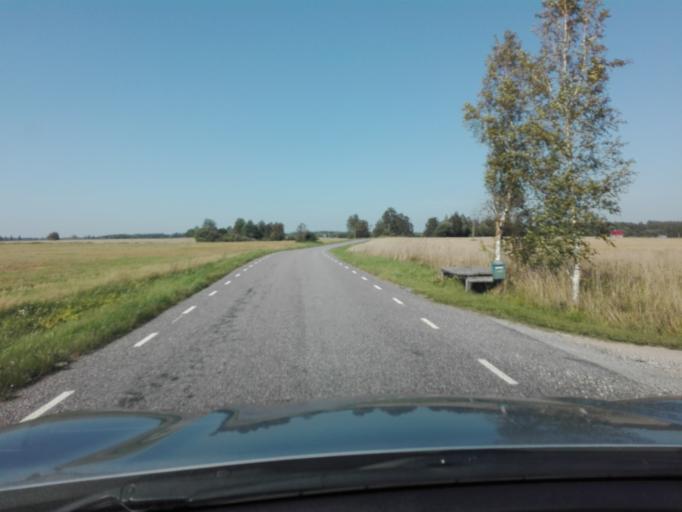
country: EE
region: Raplamaa
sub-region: Rapla vald
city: Rapla
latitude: 59.0625
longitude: 24.7602
